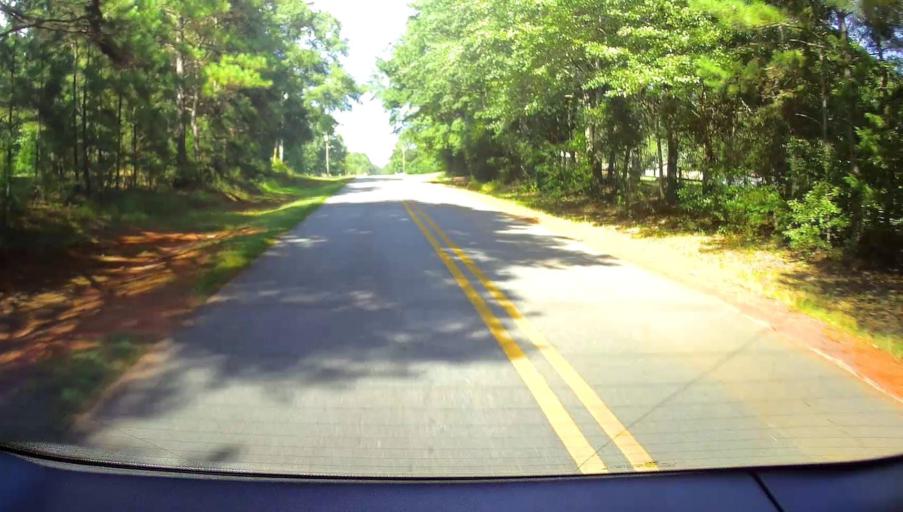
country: US
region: Georgia
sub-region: Upson County
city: Hannahs Mill
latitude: 32.9380
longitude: -84.3497
